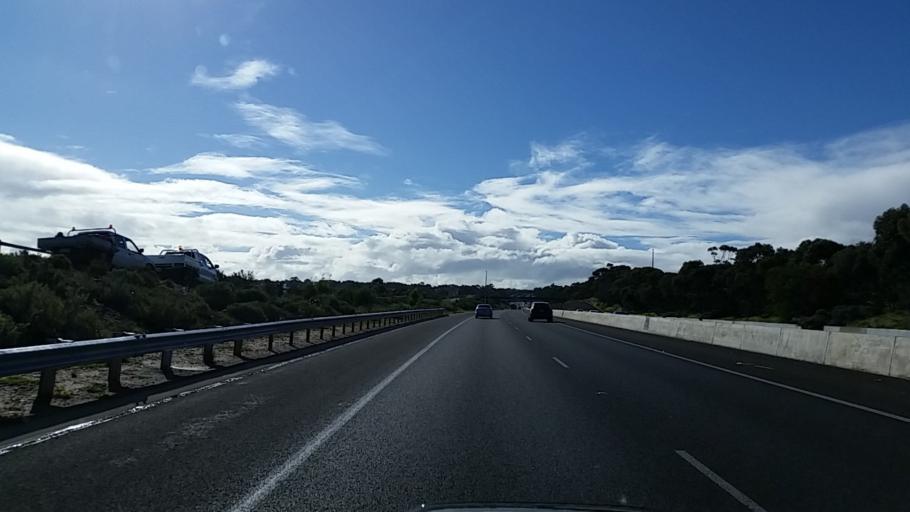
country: AU
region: South Australia
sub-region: Onkaparinga
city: Noarlunga Downs
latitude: -35.1560
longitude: 138.5059
